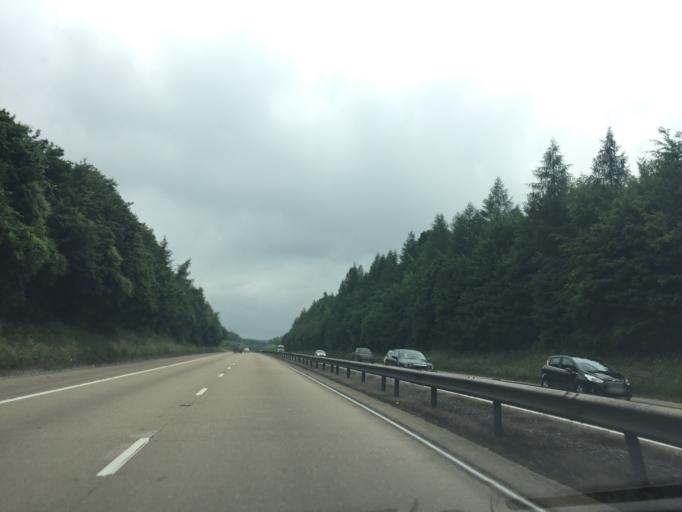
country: GB
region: England
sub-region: Hampshire
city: Kings Worthy
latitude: 51.1288
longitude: -1.2491
